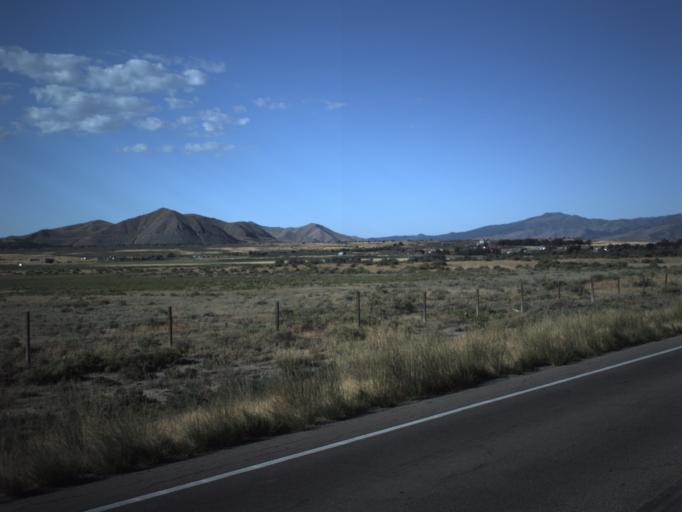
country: US
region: Utah
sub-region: Utah County
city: Genola
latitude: 39.9562
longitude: -111.8823
